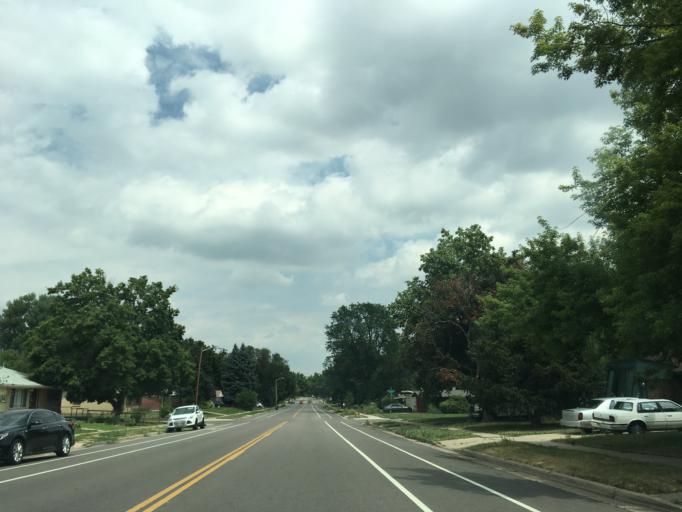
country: US
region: Colorado
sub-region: Arapahoe County
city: Sheridan
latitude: 39.6696
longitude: -105.0350
